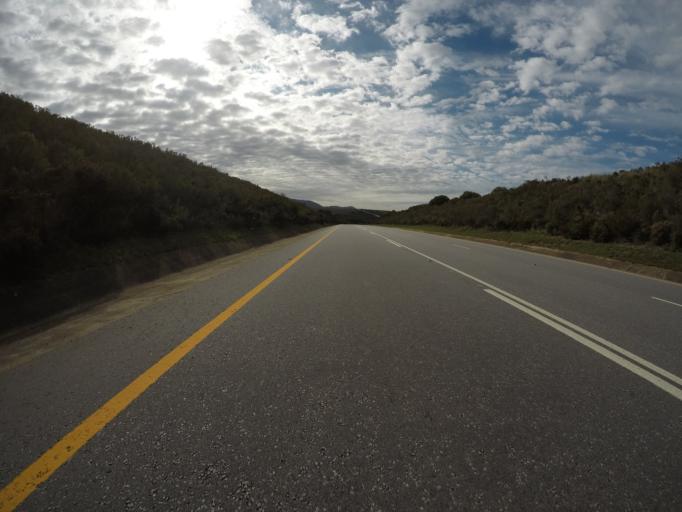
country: ZA
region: Eastern Cape
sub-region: Cacadu District Municipality
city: Kruisfontein
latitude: -34.0155
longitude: 24.6292
